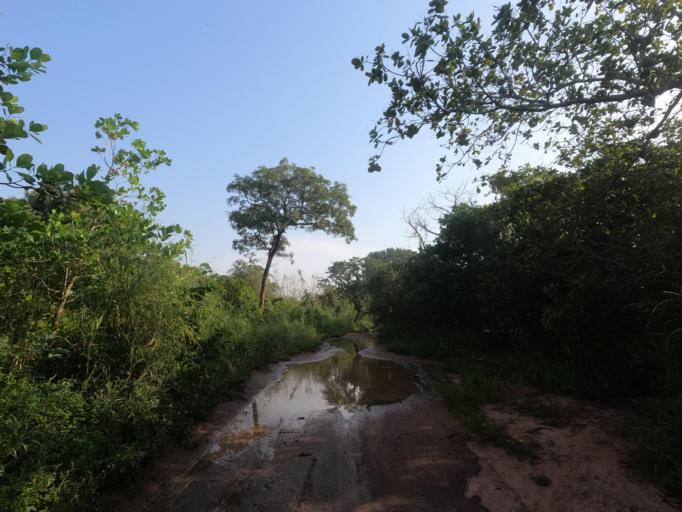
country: GW
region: Oio
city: Bissora
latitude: 12.3877
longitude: -15.7160
